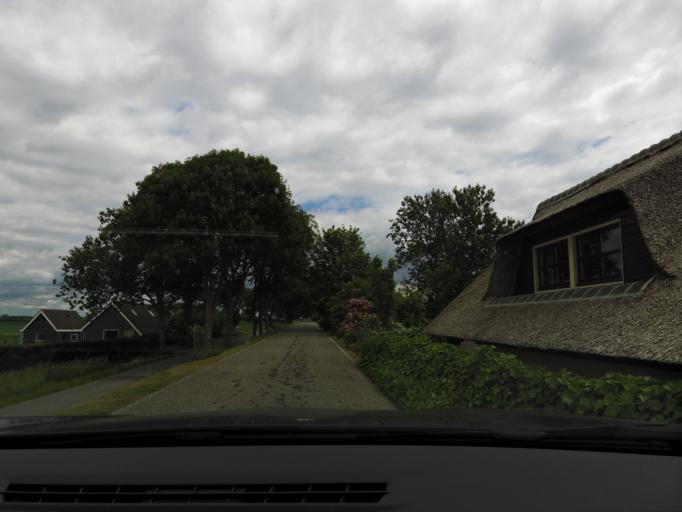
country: NL
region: North Brabant
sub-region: Gemeente Moerdijk
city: Willemstad
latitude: 51.7292
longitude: 4.4621
